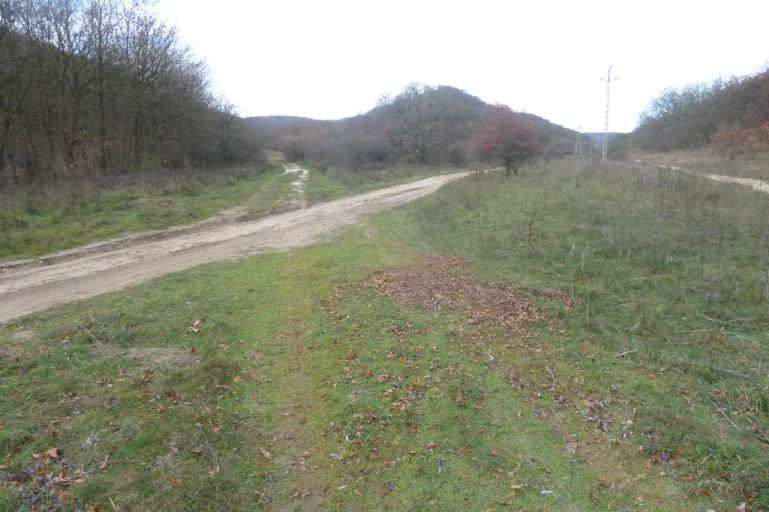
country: HU
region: Fejer
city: Zamoly
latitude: 47.3939
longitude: 18.3609
